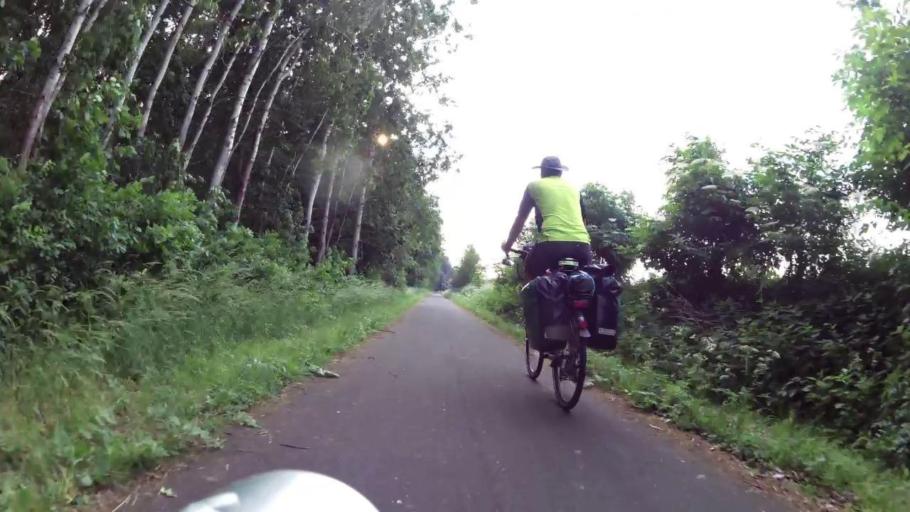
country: PL
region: Kujawsko-Pomorskie
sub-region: Powiat chelminski
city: Unislaw
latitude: 53.1855
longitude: 18.3820
